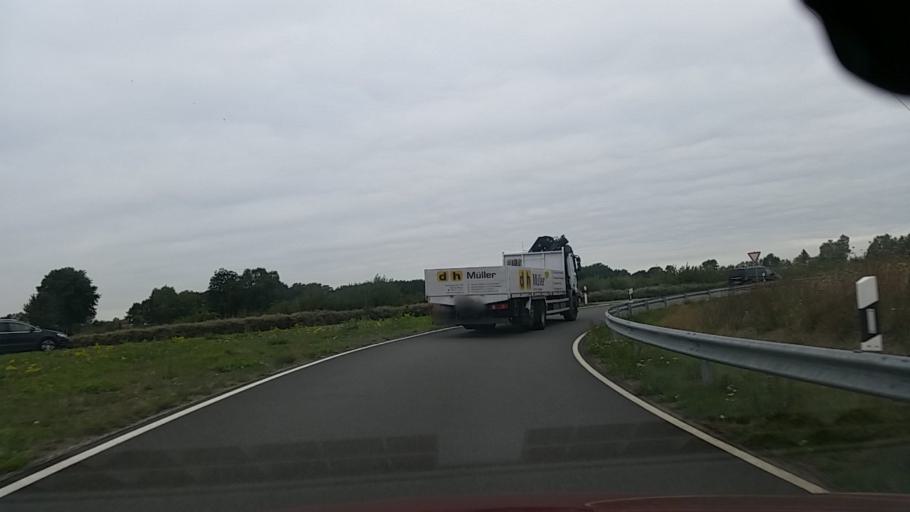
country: DE
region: Lower Saxony
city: Wagenhoff
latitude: 52.5060
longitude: 10.5257
